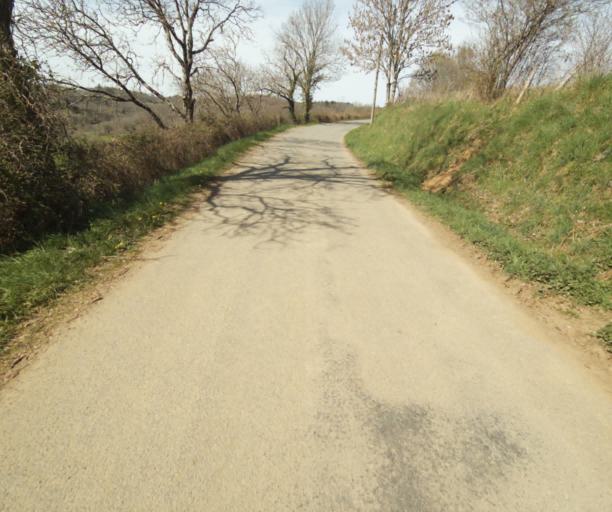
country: FR
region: Limousin
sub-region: Departement de la Correze
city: Seilhac
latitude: 45.3883
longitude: 1.7811
